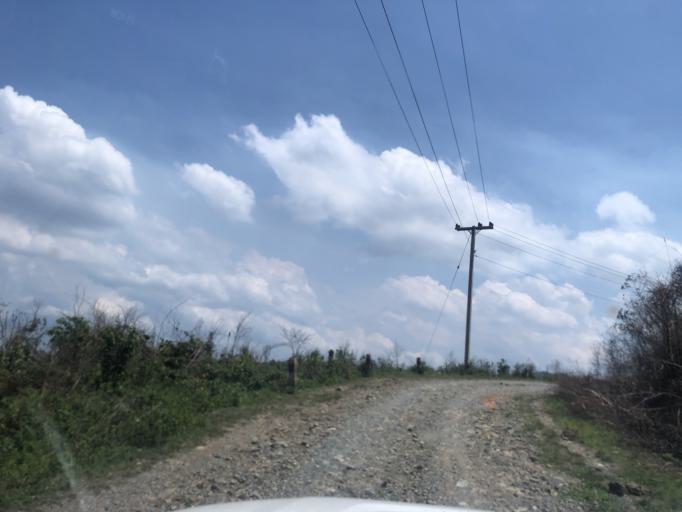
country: LA
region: Phongsali
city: Phongsali
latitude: 21.4201
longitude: 102.1848
